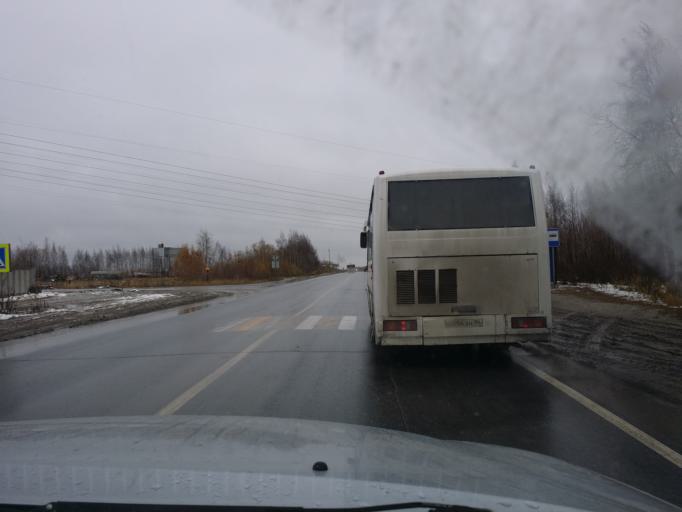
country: RU
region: Khanty-Mansiyskiy Avtonomnyy Okrug
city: Megion
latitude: 61.0511
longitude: 76.1123
